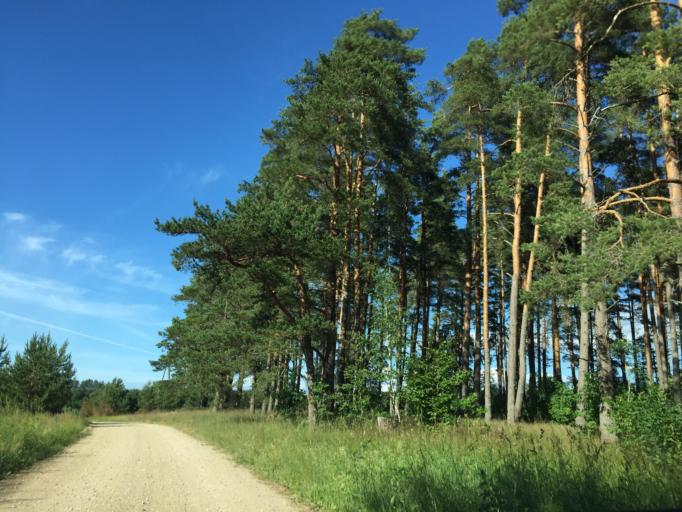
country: LV
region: Kuldigas Rajons
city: Kuldiga
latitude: 57.0683
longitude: 21.8252
